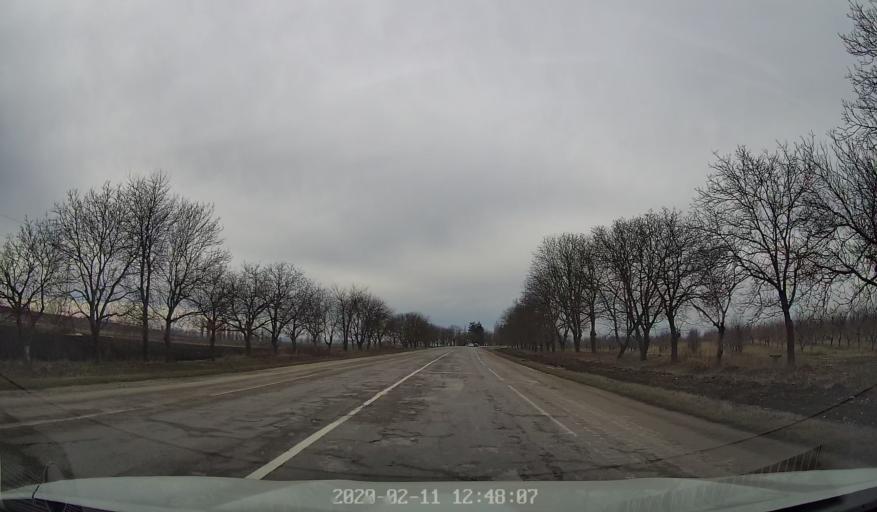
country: MD
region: Briceni
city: Briceni
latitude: 48.2778
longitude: 27.1524
